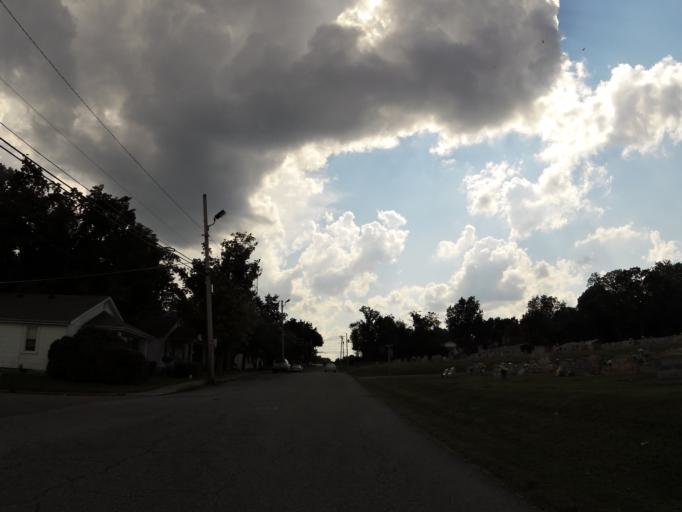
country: US
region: Tennessee
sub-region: Dickson County
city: Dickson
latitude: 36.0799
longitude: -87.3867
